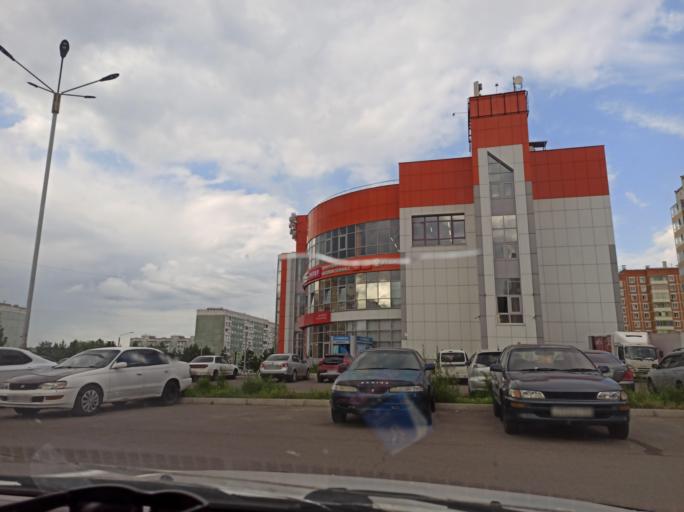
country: RU
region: Krasnoyarskiy
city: Sosnovoborsk
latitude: 56.1157
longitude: 93.3304
